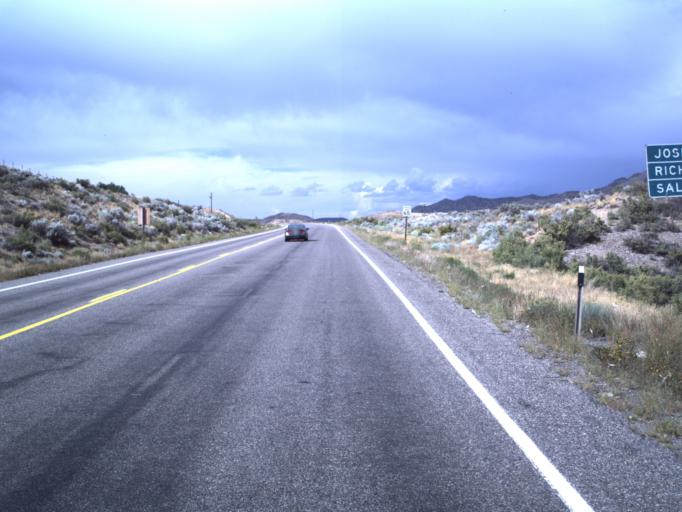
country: US
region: Utah
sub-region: Sevier County
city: Monroe
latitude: 38.4539
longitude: -112.2306
